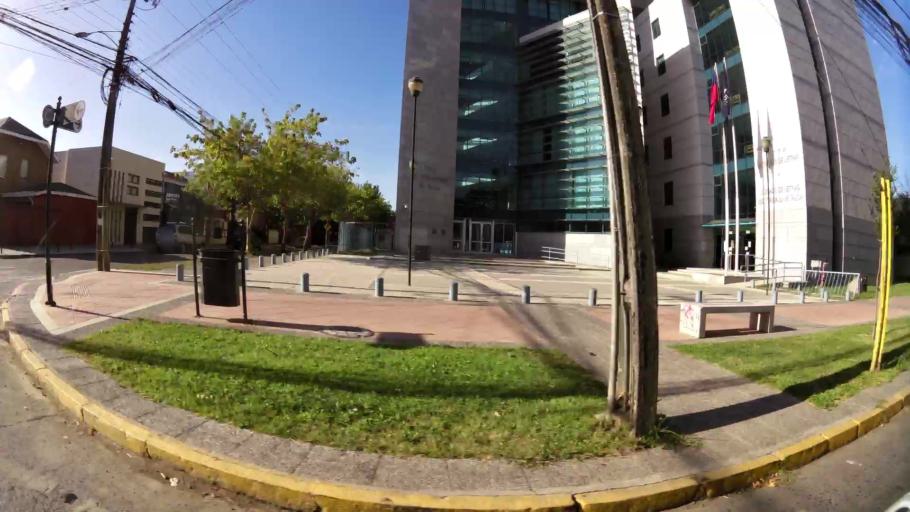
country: CL
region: Maule
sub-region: Provincia de Talca
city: Talca
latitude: -35.4215
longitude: -71.6676
